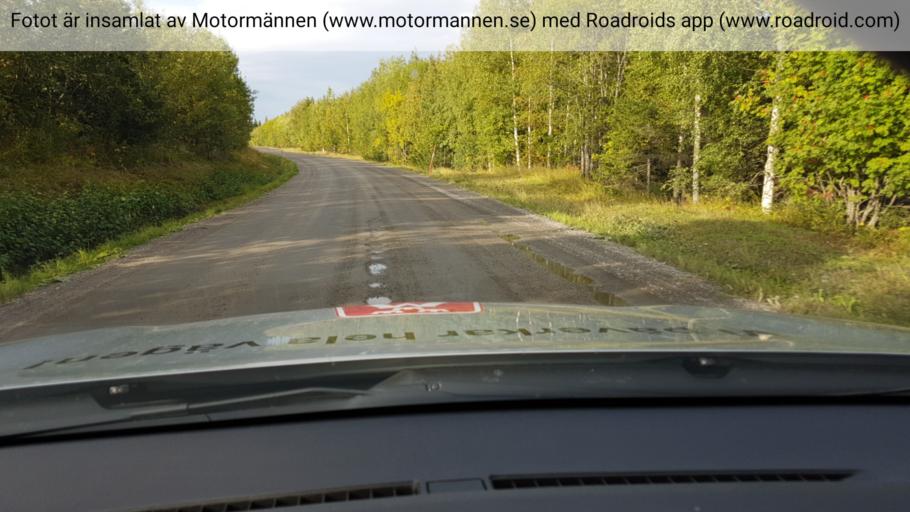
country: SE
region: Jaemtland
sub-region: Stroemsunds Kommun
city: Stroemsund
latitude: 64.0145
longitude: 15.8145
